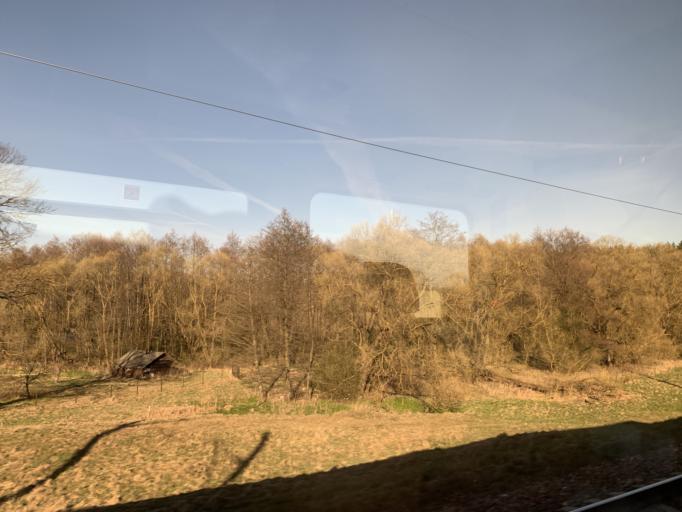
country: BY
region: Grodnenskaya
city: Smarhon'
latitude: 54.4317
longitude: 26.5224
